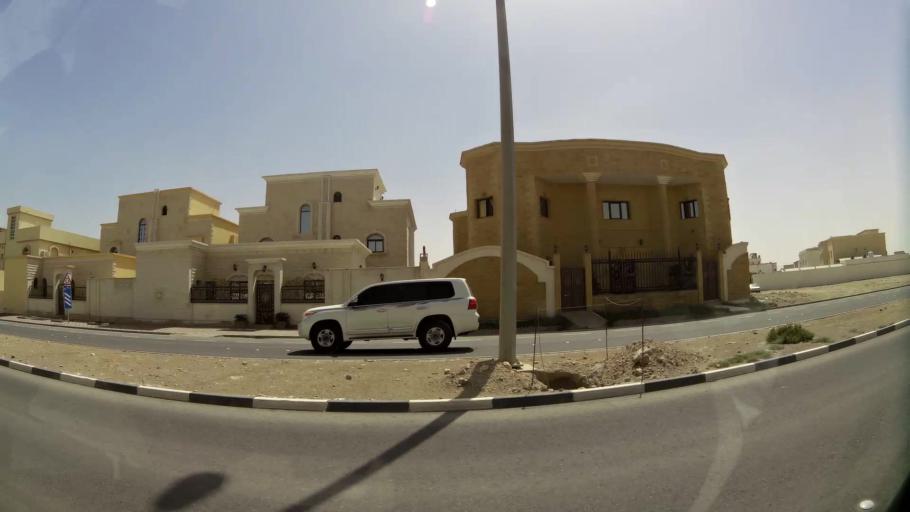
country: QA
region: Baladiyat Umm Salal
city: Umm Salal Muhammad
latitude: 25.3662
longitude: 51.4277
